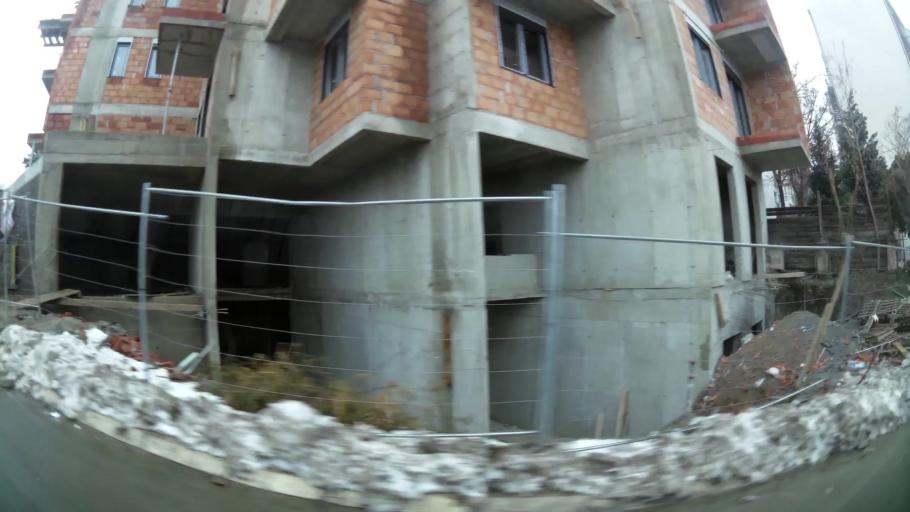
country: RS
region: Central Serbia
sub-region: Belgrade
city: Cukarica
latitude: 44.7846
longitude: 20.4233
